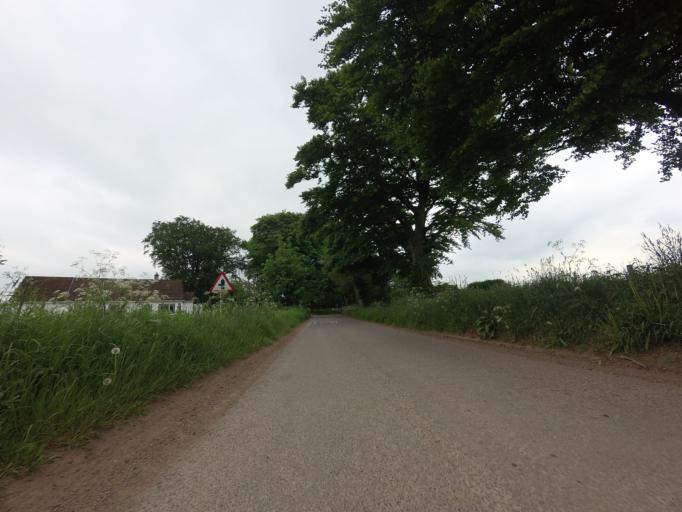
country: GB
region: Scotland
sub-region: Perth and Kinross
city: Kinross
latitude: 56.1746
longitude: -3.4397
